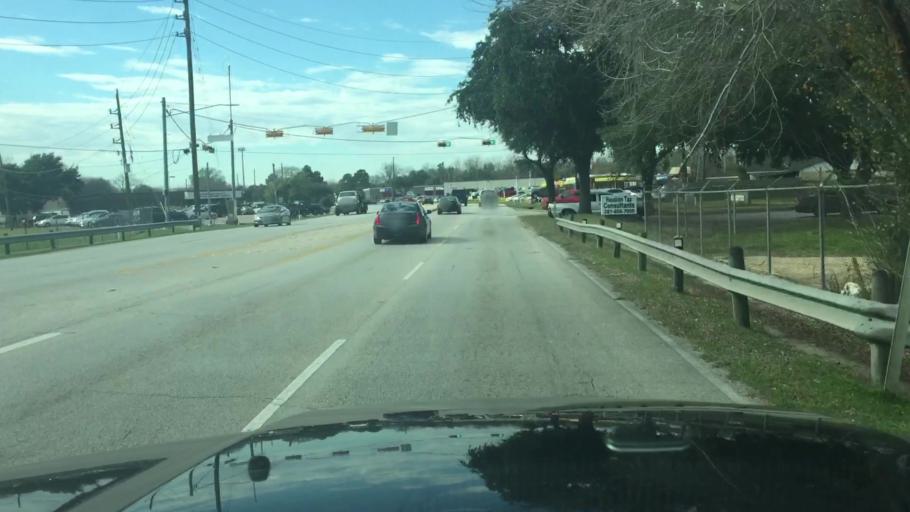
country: US
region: Texas
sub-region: Harris County
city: Oak Cliff Place
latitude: 29.8352
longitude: -95.6545
